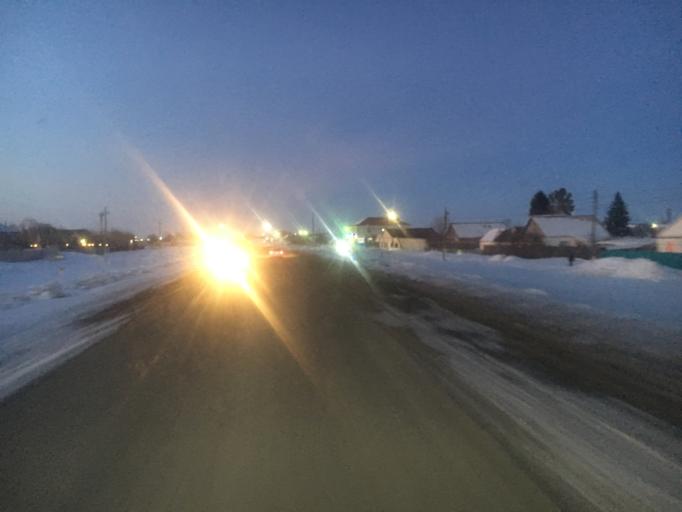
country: KZ
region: Batys Qazaqstan
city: Oral
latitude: 51.1486
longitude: 51.4886
